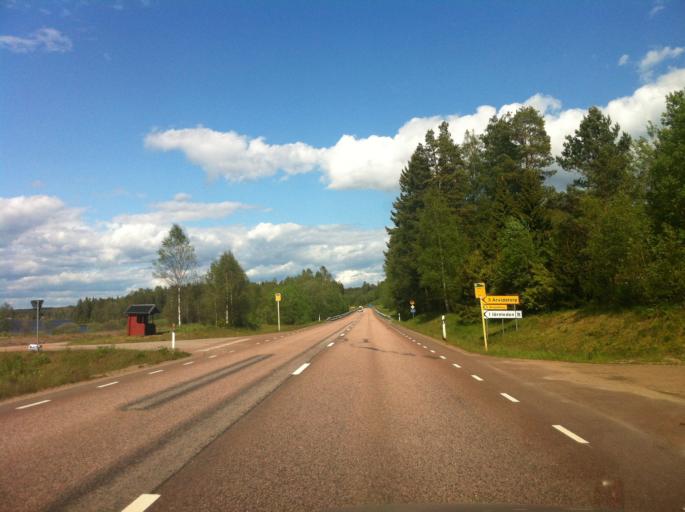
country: SE
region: Vaermland
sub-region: Kristinehamns Kommun
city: Kristinehamn
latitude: 59.3868
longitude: 14.1866
